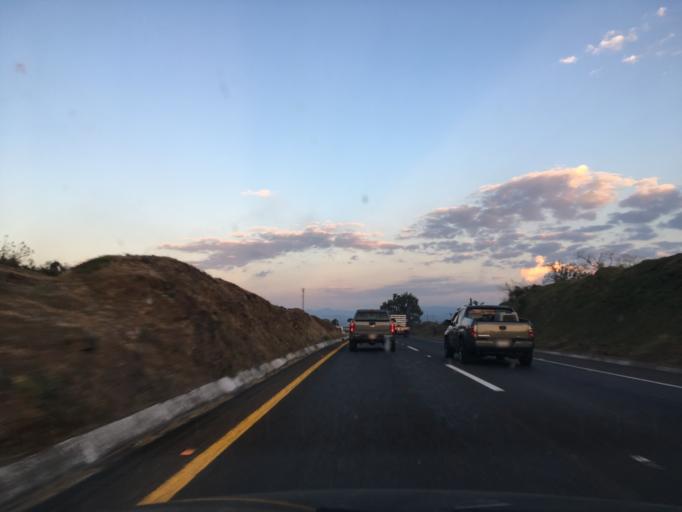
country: MX
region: Michoacan
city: Lagunillas
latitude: 19.5524
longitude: -101.3590
